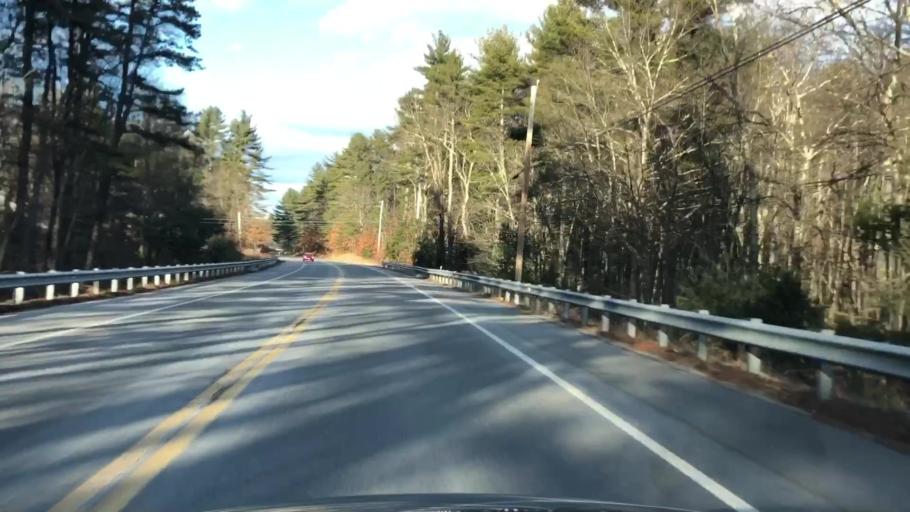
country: US
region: New Hampshire
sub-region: Hillsborough County
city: Brookline
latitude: 42.7157
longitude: -71.6627
